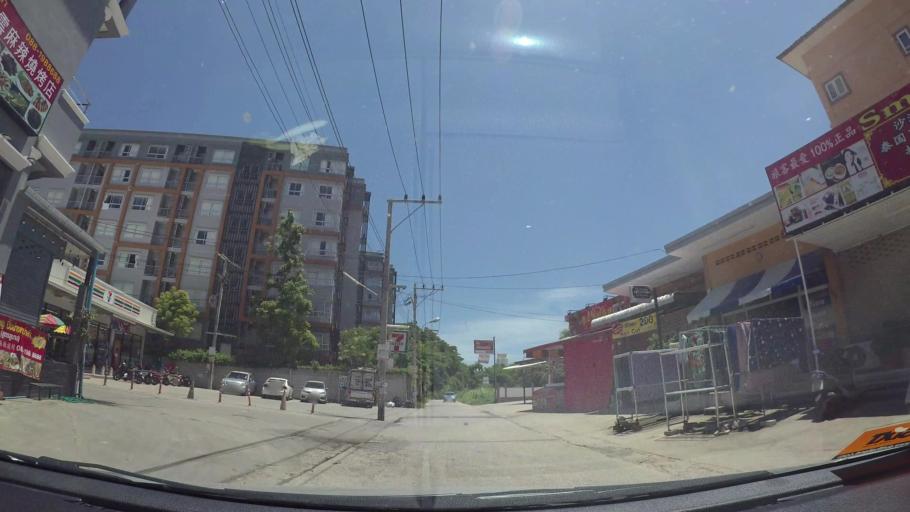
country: TH
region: Chon Buri
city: Phatthaya
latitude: 12.9203
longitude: 100.8929
